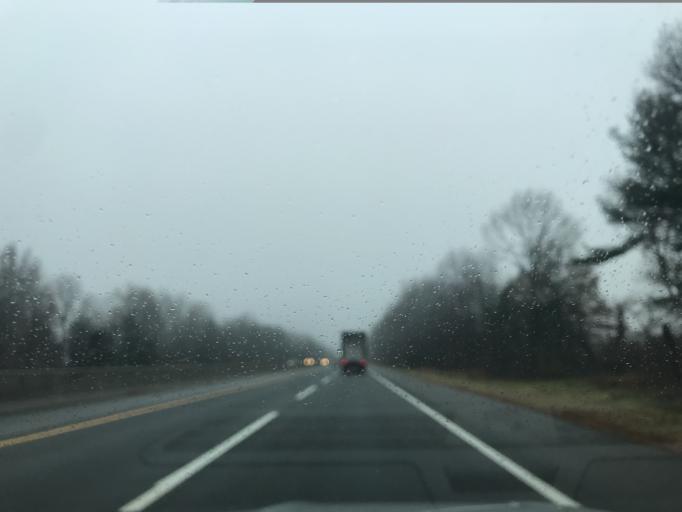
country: US
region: New Jersey
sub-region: Gloucester County
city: Mullica Hill
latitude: 39.7721
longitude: -75.2455
